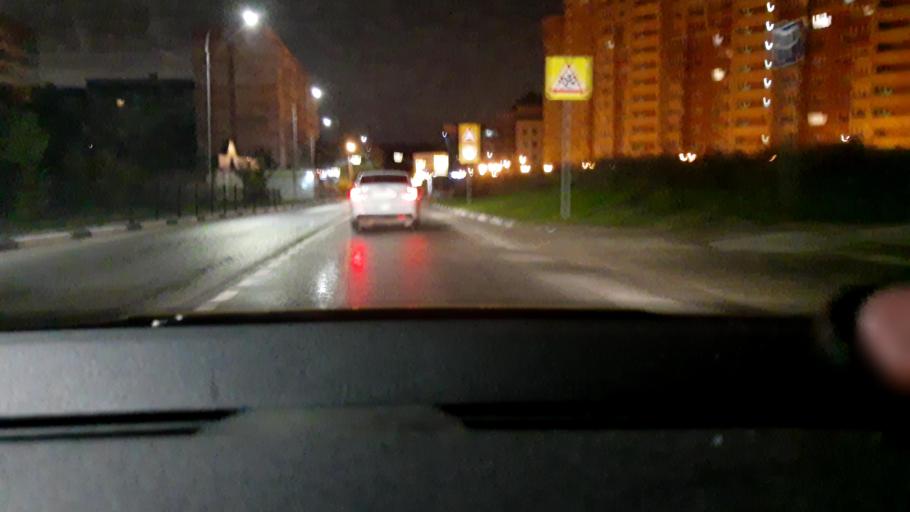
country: RU
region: Moskovskaya
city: Krasnogorsk
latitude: 55.8305
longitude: 37.2956
